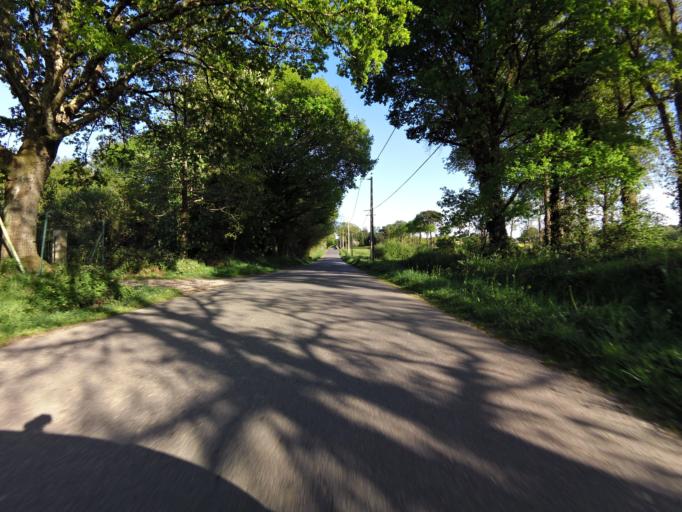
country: FR
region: Brittany
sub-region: Departement du Morbihan
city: Molac
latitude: 47.7417
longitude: -2.4565
